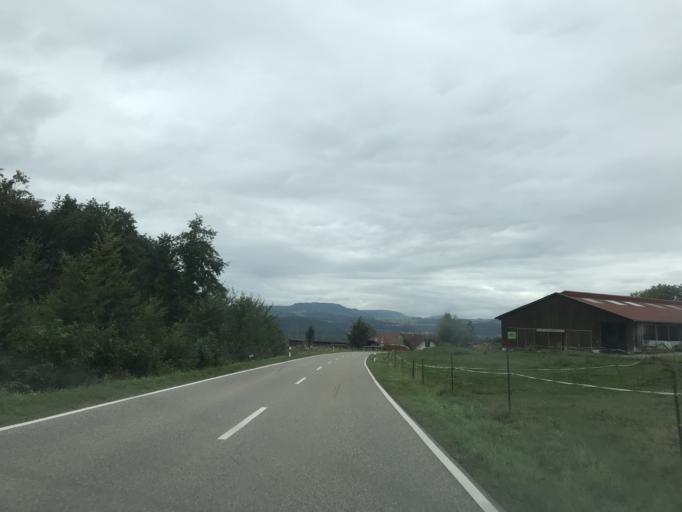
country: DE
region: Baden-Wuerttemberg
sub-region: Freiburg Region
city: Laufenburg
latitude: 47.5741
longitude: 8.0385
